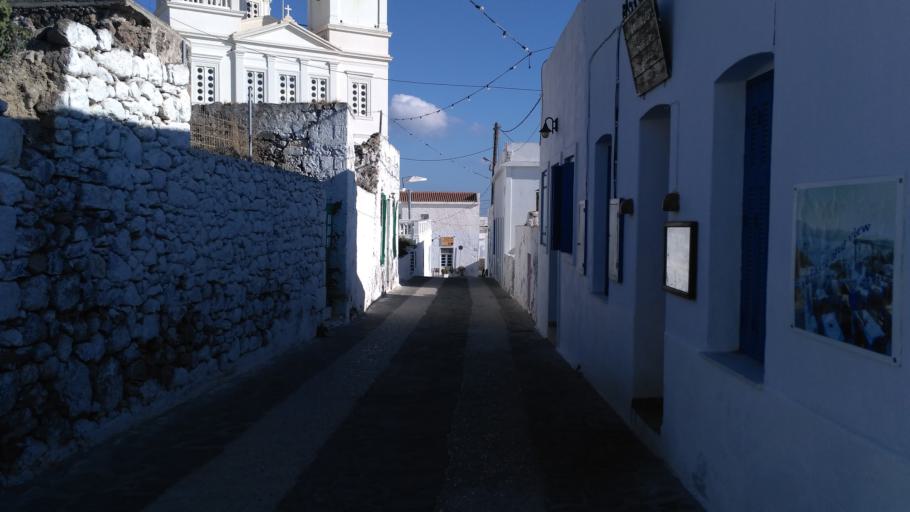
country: GR
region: South Aegean
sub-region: Nomos Kykladon
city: Milos
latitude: 36.7387
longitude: 24.4261
